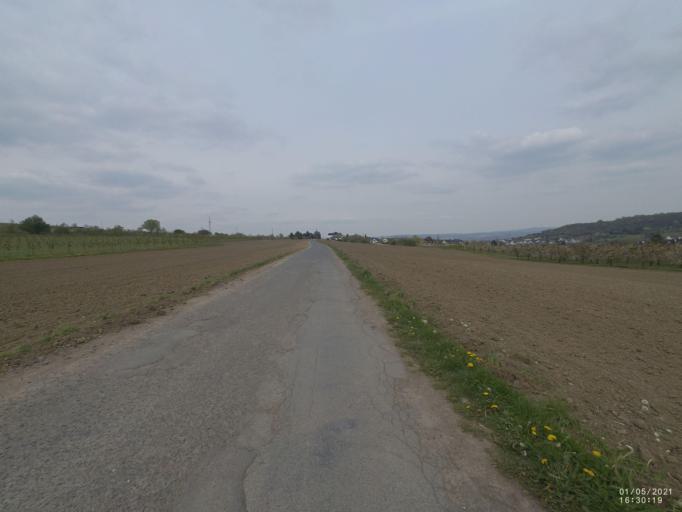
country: DE
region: Rheinland-Pfalz
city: Mulheim-Karlich
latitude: 50.3803
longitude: 7.4843
